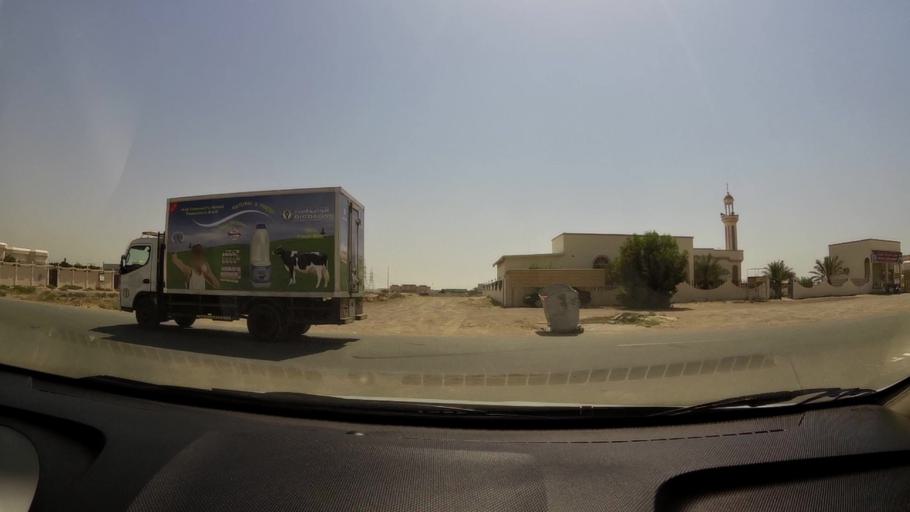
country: AE
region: Umm al Qaywayn
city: Umm al Qaywayn
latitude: 25.4906
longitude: 55.5847
